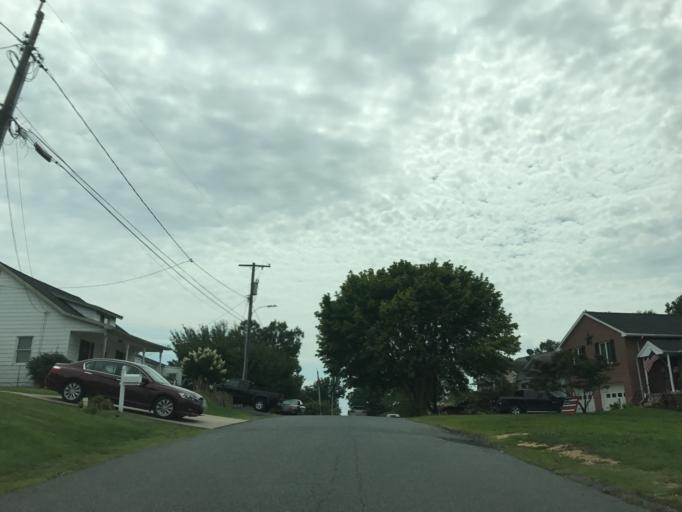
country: US
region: Maryland
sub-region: Baltimore County
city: Rosedale
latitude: 39.2901
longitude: -76.5124
